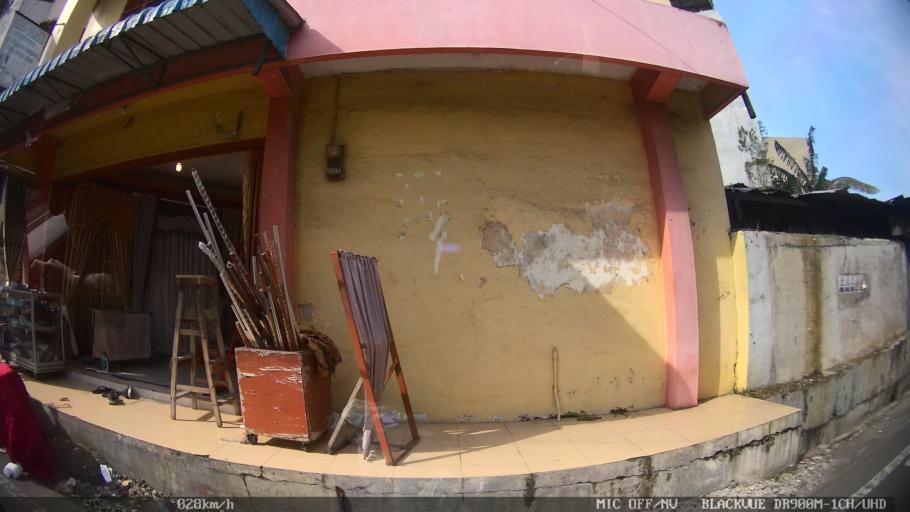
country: ID
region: North Sumatra
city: Binjai
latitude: 3.6045
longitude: 98.4866
